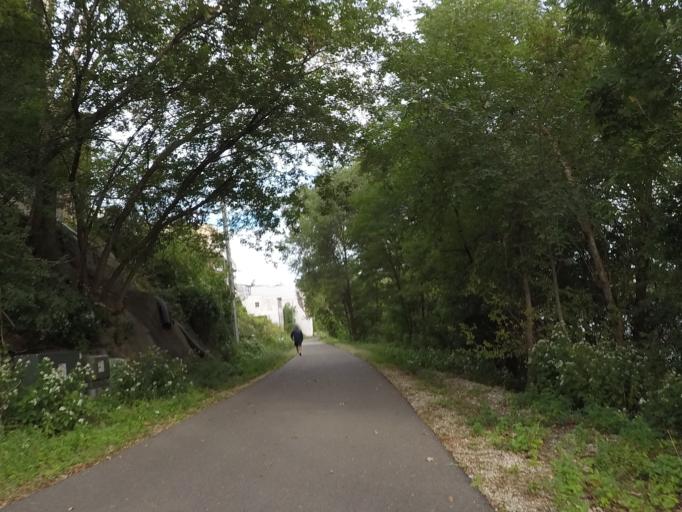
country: US
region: Wisconsin
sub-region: Sauk County
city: Prairie du Sac
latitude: 43.2918
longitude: -89.7207
